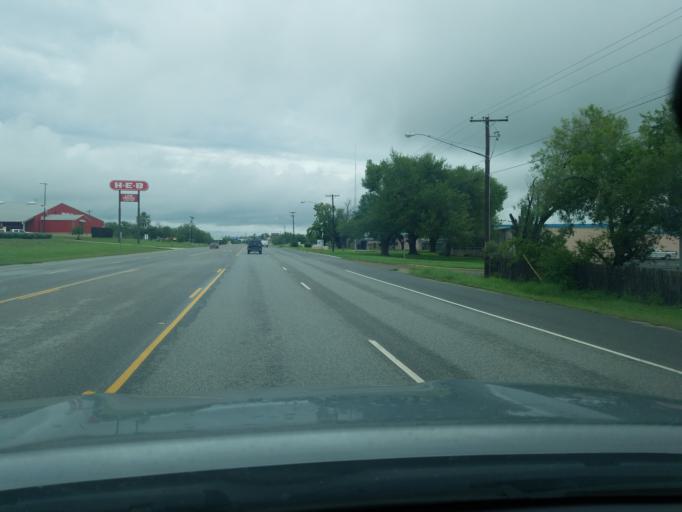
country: US
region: Texas
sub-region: Dimmit County
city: Carrizo Springs
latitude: 28.5353
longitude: -99.8512
